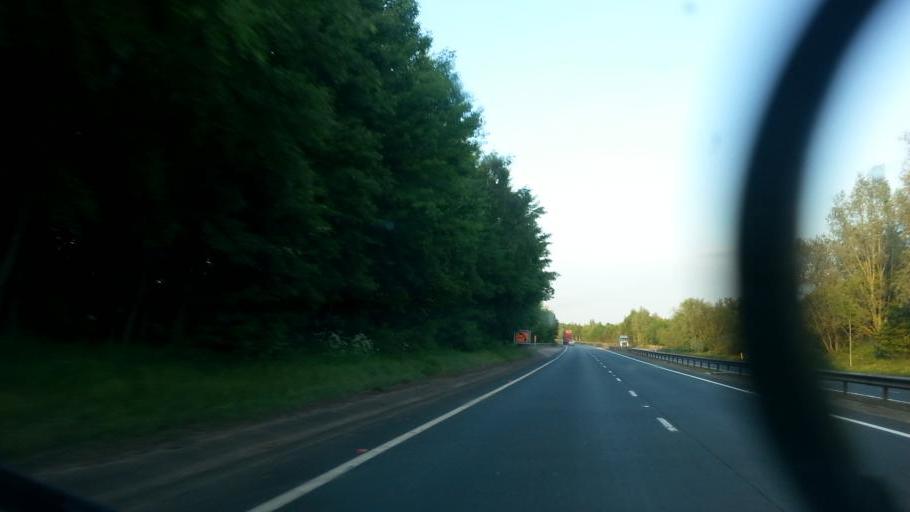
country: GB
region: England
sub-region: Derbyshire
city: Etwall
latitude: 52.8786
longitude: -1.6518
